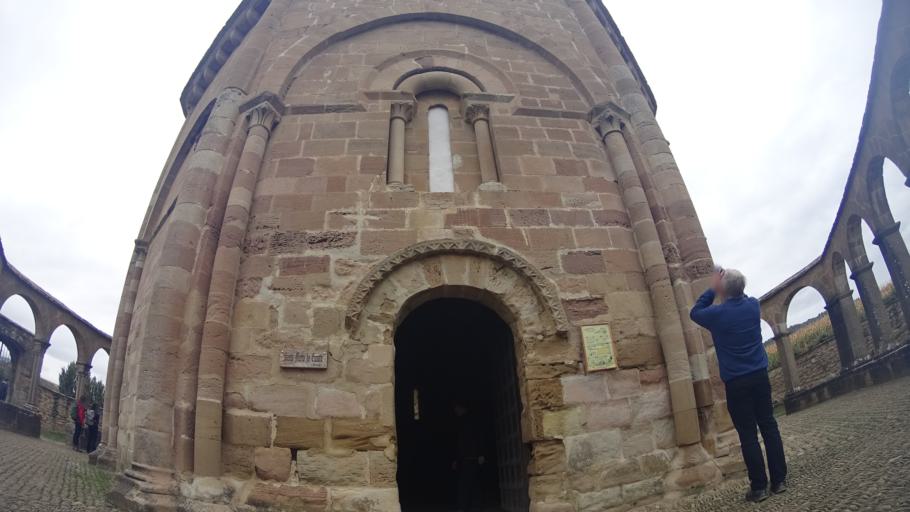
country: ES
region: Navarre
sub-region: Provincia de Navarra
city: Muruzabal
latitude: 42.6723
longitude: -1.7616
